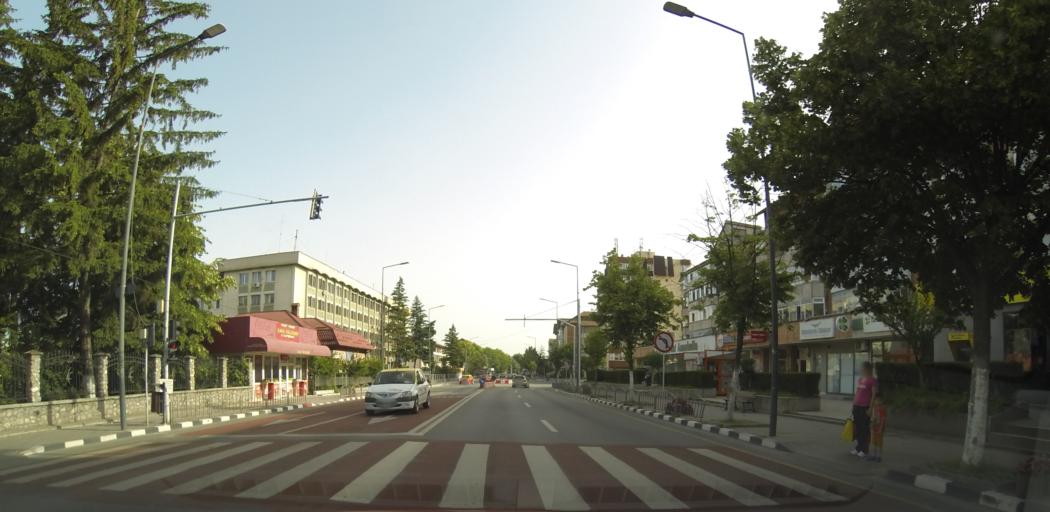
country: RO
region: Valcea
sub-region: Municipiul Ramnicu Valcea
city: Ramnicu Valcea
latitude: 45.0952
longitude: 24.3614
